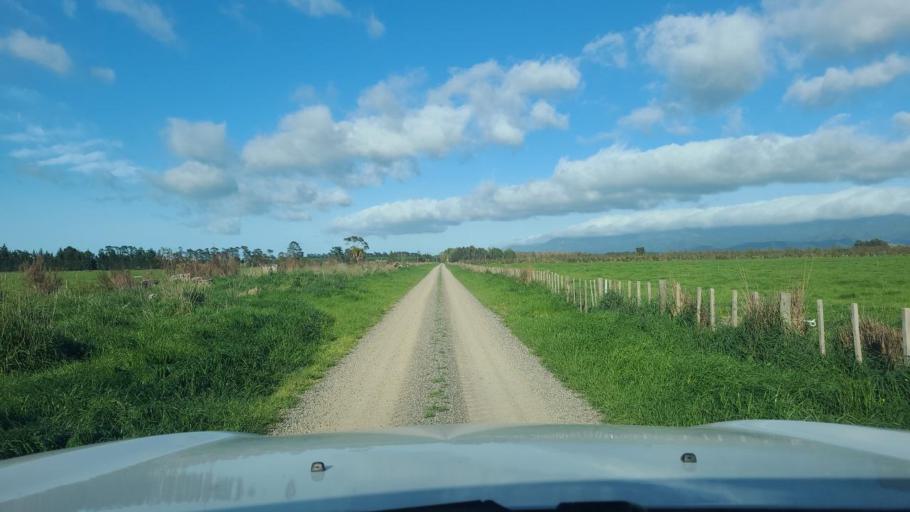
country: NZ
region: Wellington
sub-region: Upper Hutt City
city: Upper Hutt
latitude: -41.2973
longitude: 175.2697
